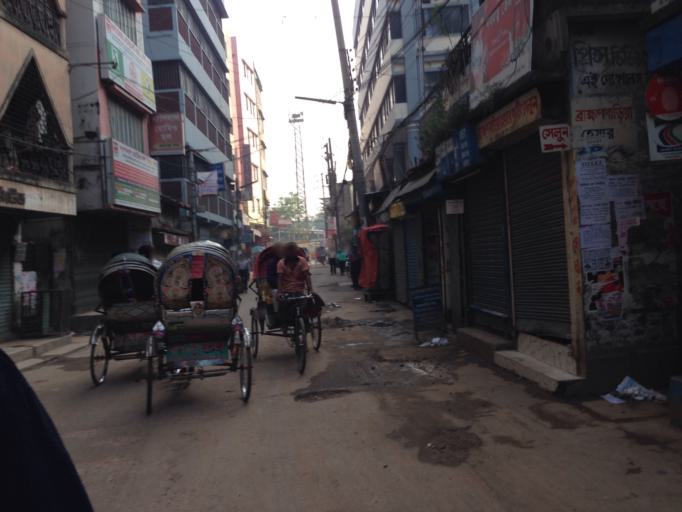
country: BD
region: Dhaka
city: Paltan
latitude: 23.7291
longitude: 90.4247
